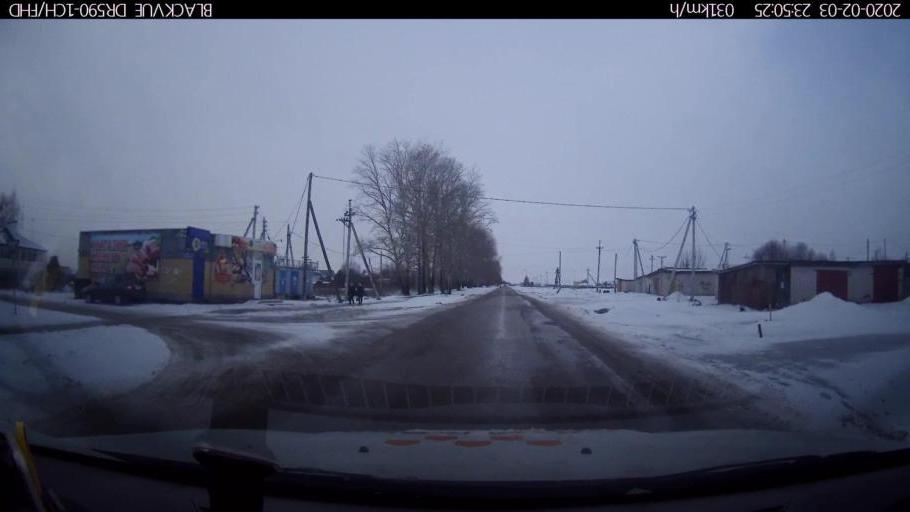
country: RU
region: Nizjnij Novgorod
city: Dal'neye Konstantinovo
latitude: 55.8068
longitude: 44.0785
